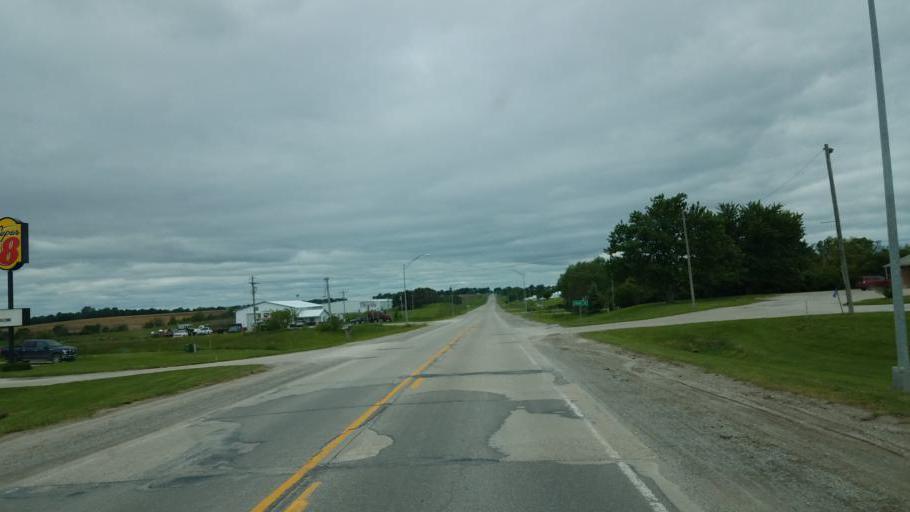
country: US
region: Iowa
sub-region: Decatur County
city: Lamoni
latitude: 40.6237
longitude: -93.8978
